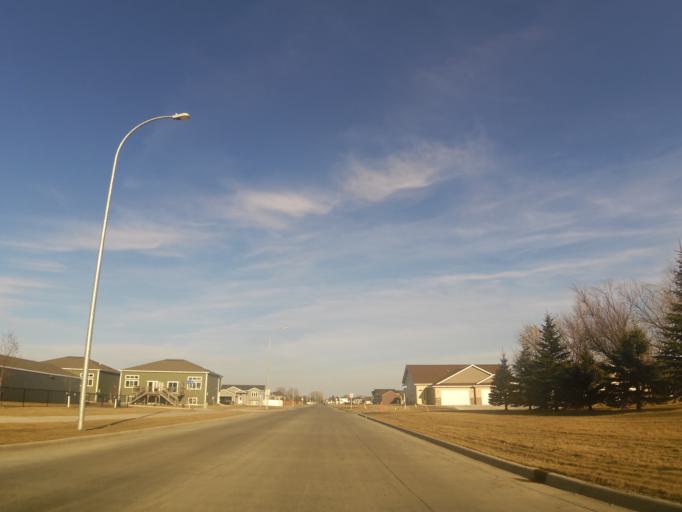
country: US
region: North Dakota
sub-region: Grand Forks County
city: Grand Forks
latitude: 47.8676
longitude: -97.0431
